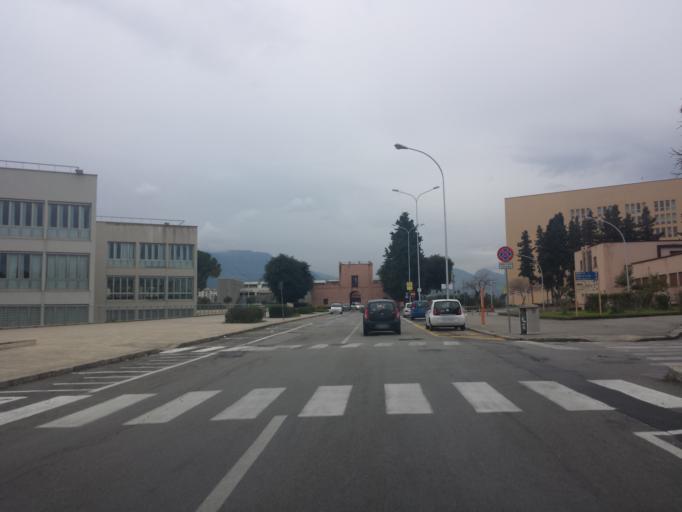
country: IT
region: Sicily
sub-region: Palermo
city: Palermo
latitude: 38.1025
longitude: 13.3472
